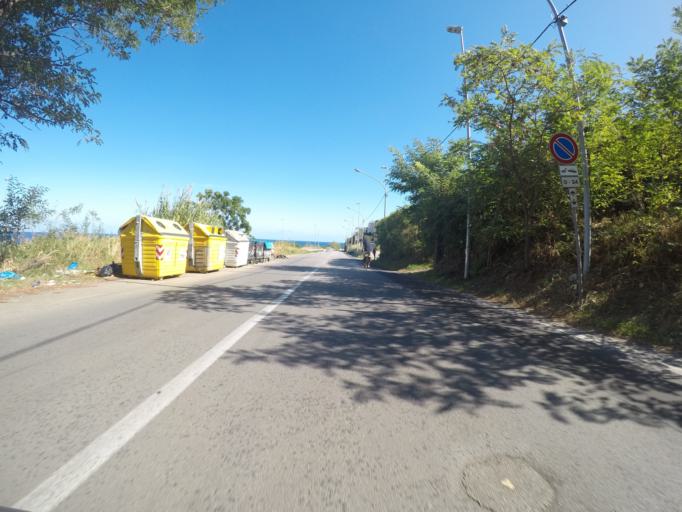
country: IT
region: Sicily
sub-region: Palermo
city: Palermo
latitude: 38.1898
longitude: 13.3549
